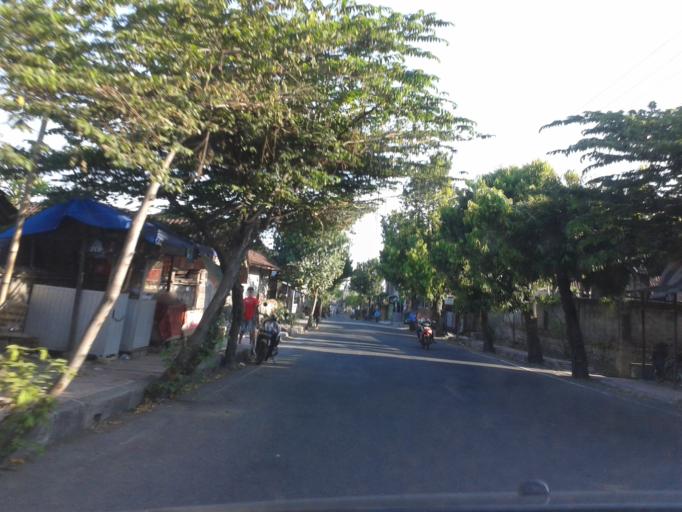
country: ID
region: Bali
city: Klungkung
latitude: -8.5196
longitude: 115.4011
